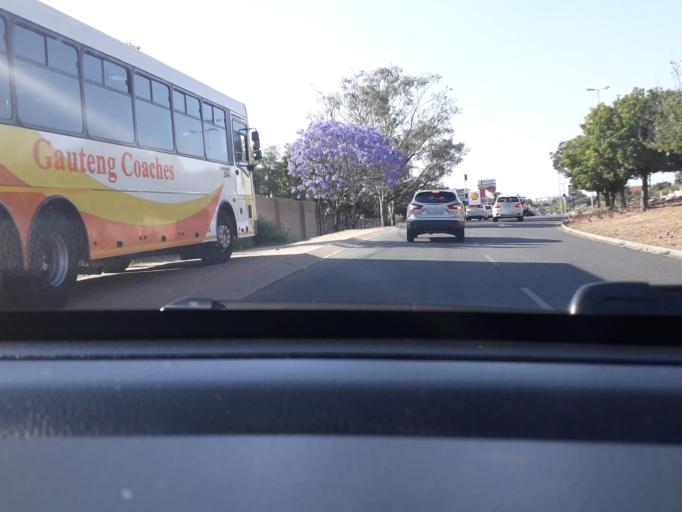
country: ZA
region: Gauteng
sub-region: City of Johannesburg Metropolitan Municipality
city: Midrand
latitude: -26.0391
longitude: 28.0806
